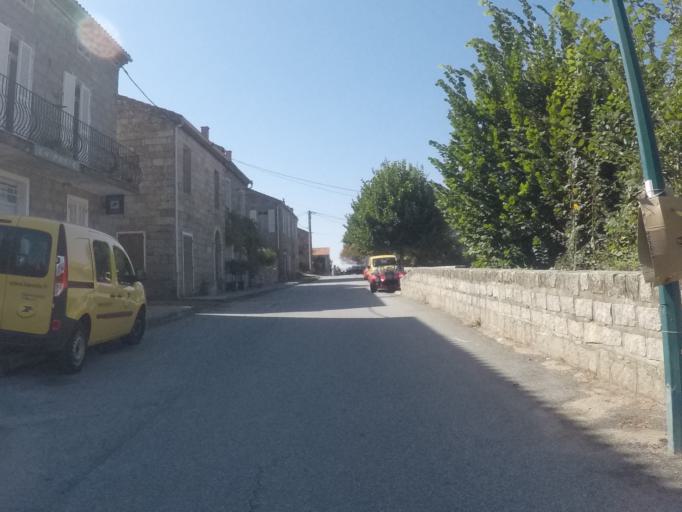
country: FR
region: Corsica
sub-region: Departement de la Corse-du-Sud
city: Zonza
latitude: 41.7700
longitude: 9.0802
